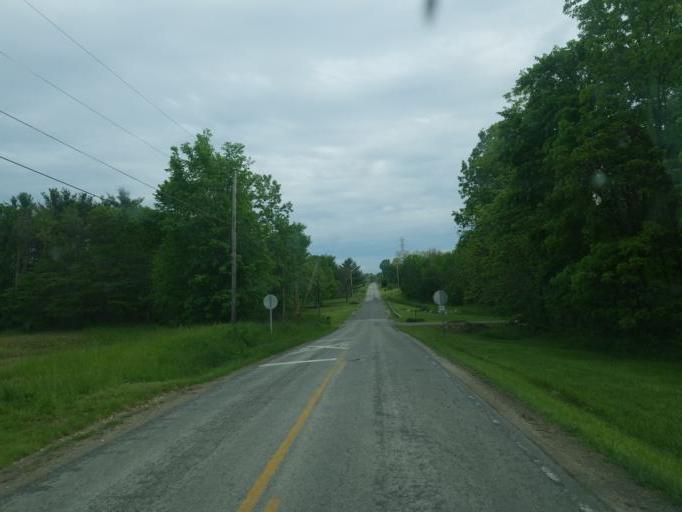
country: US
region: Ohio
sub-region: Richland County
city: Ontario
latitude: 40.8075
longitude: -82.6285
